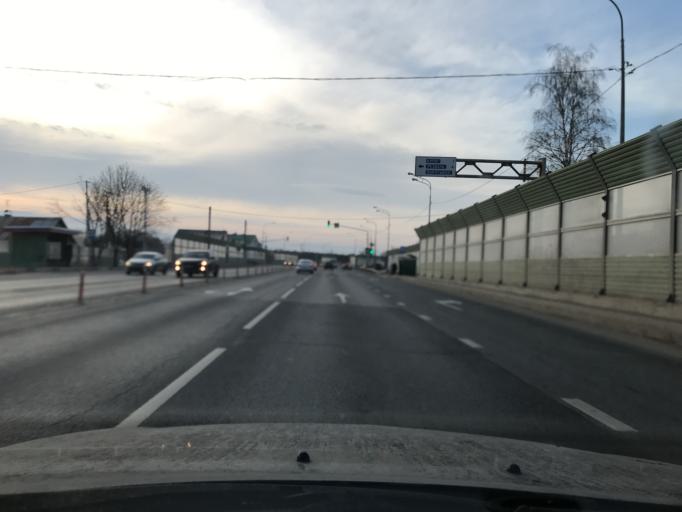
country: RU
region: Kaluga
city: Mstikhino
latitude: 54.5571
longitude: 36.1279
